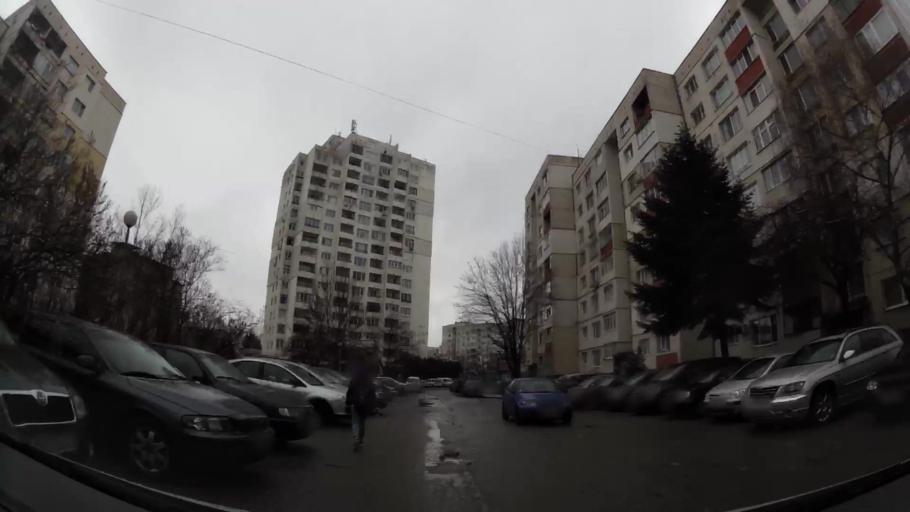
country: BG
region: Sofia-Capital
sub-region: Stolichna Obshtina
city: Sofia
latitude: 42.6410
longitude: 23.3750
